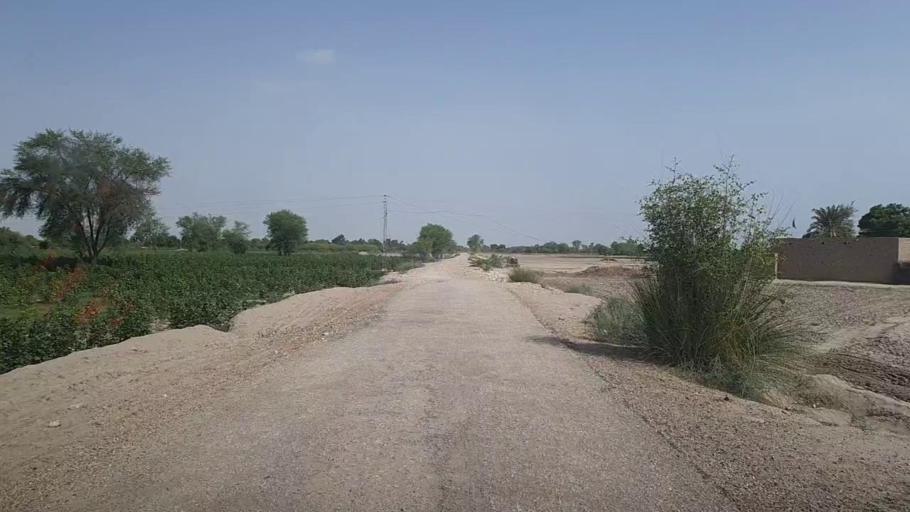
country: PK
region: Sindh
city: Pad Idan
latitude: 26.7581
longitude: 68.3400
